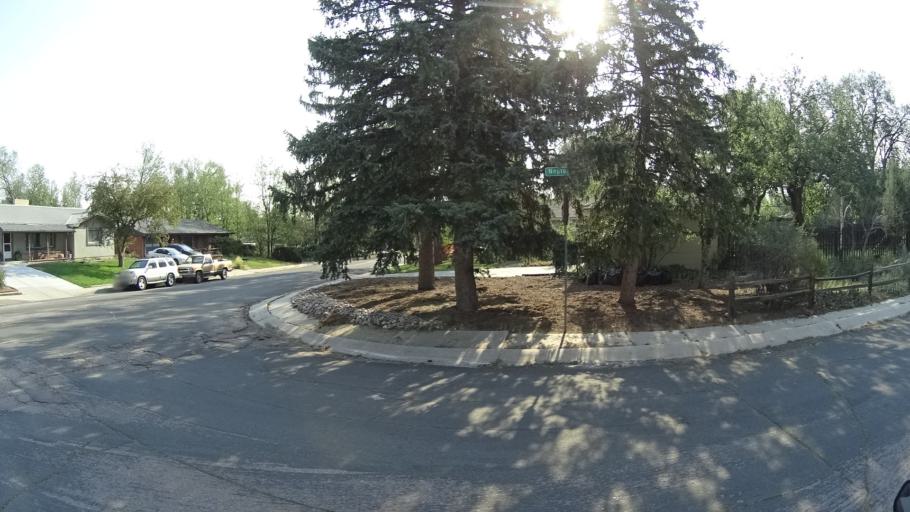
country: US
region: Colorado
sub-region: El Paso County
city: Colorado Springs
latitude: 38.8055
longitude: -104.8483
